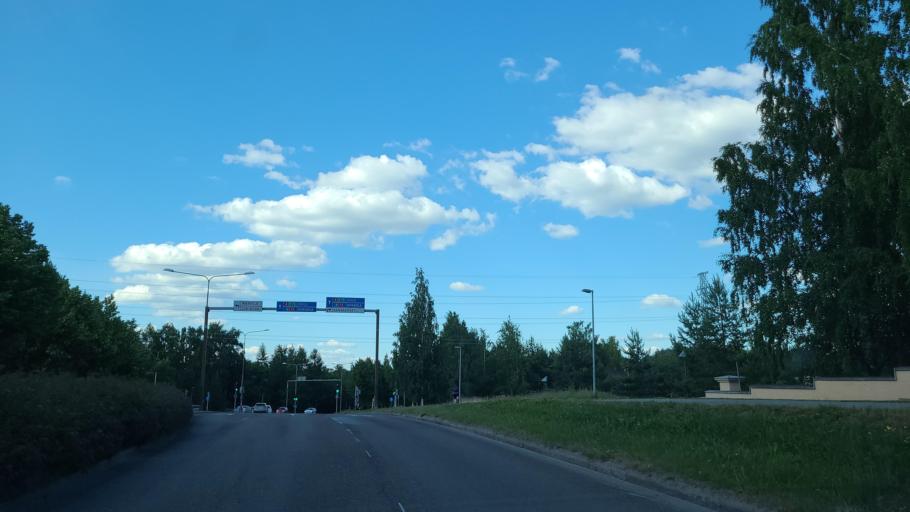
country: FI
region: Central Finland
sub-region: Jyvaeskylae
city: Jyvaeskylae
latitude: 62.2536
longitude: 25.7503
